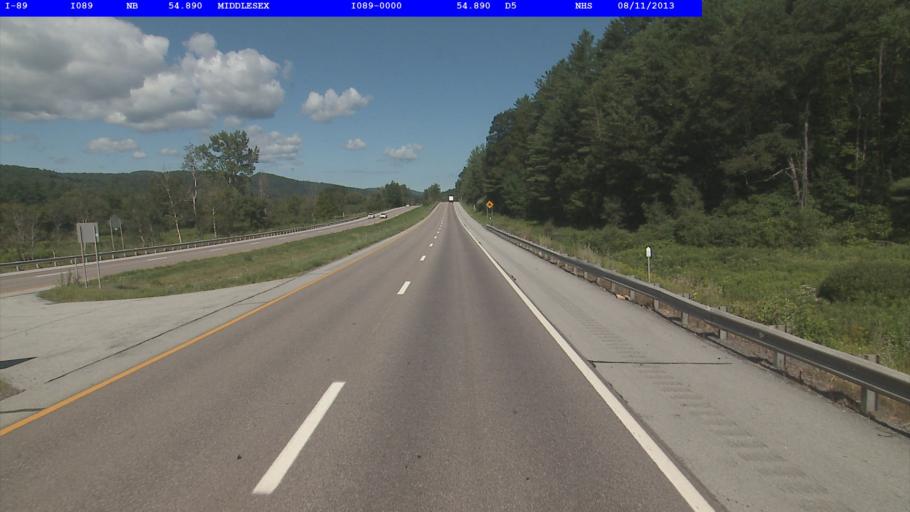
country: US
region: Vermont
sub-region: Washington County
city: Montpelier
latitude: 44.2673
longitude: -72.6245
